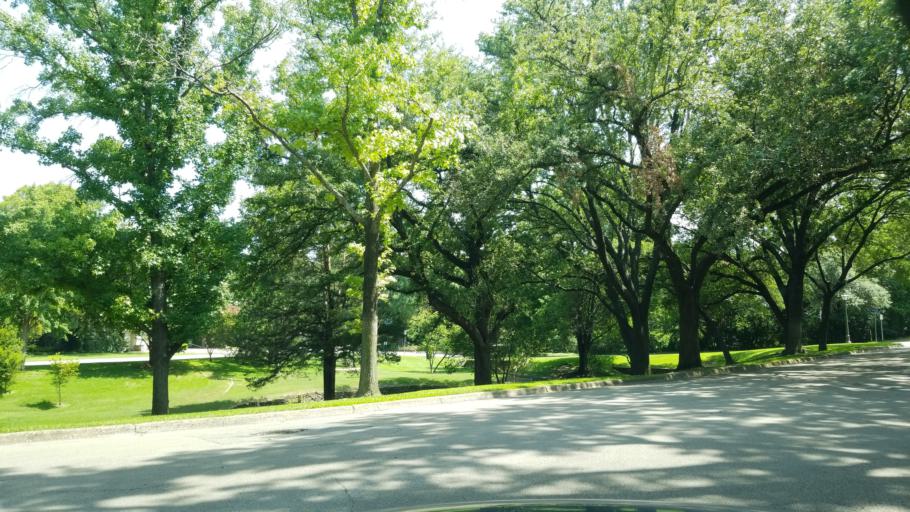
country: US
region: Texas
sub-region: Dallas County
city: Highland Park
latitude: 32.8314
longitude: -96.7947
